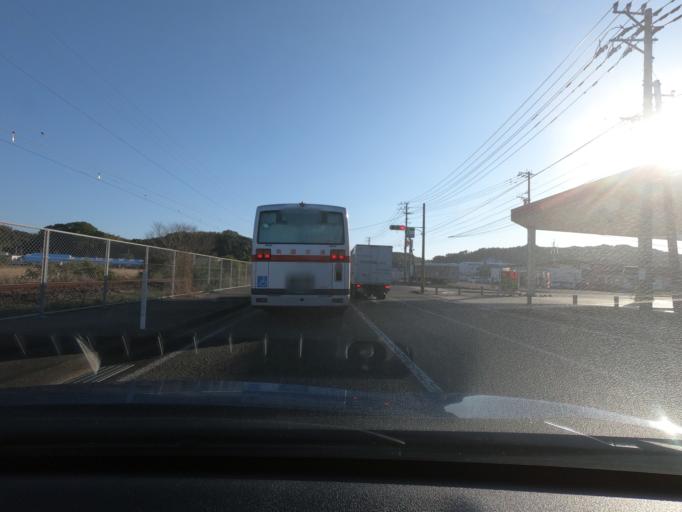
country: JP
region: Kagoshima
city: Akune
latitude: 32.0046
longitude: 130.1963
